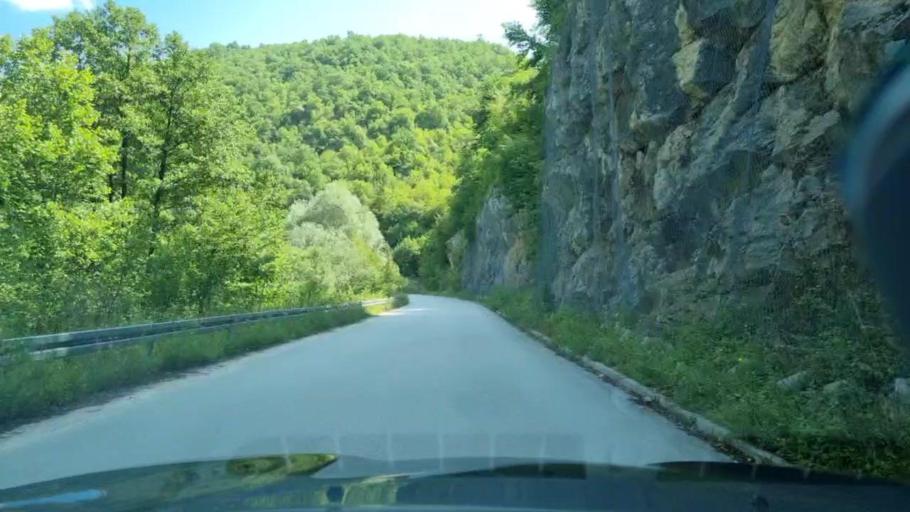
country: BA
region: Federation of Bosnia and Herzegovina
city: Kljuc
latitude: 44.5556
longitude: 16.8263
